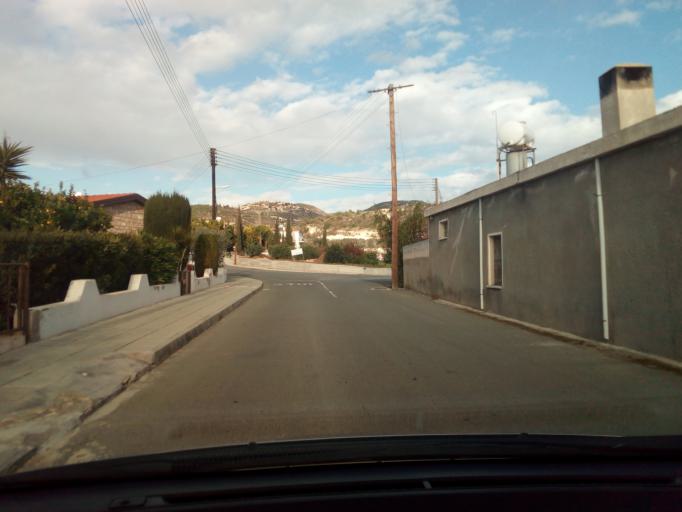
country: CY
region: Pafos
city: Mesogi
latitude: 34.8161
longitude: 32.4596
